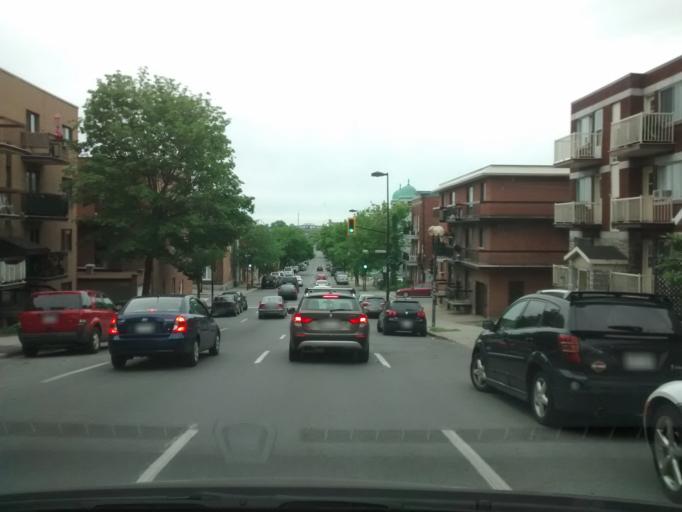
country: CA
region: Quebec
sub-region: Montreal
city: Montreal
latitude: 45.5353
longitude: -73.5599
